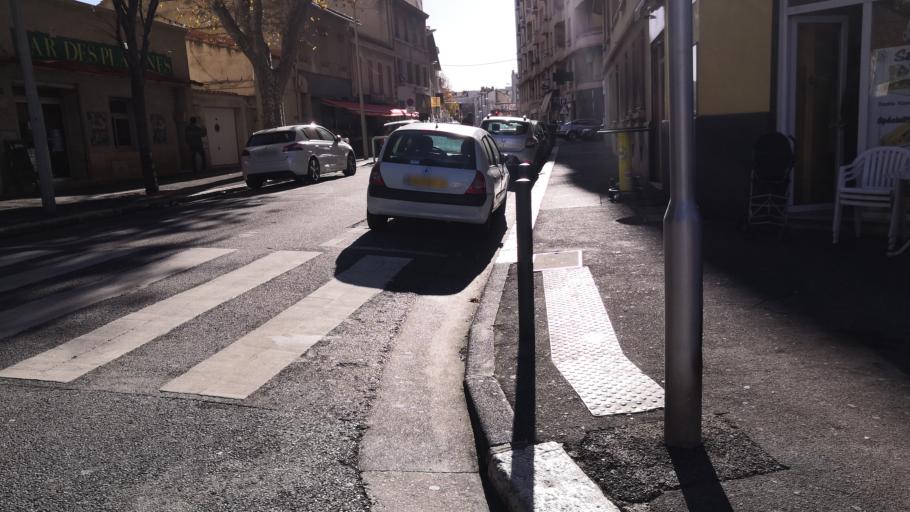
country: FR
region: Provence-Alpes-Cote d'Azur
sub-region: Departement des Bouches-du-Rhone
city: Marseille 04
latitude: 43.2991
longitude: 5.4037
